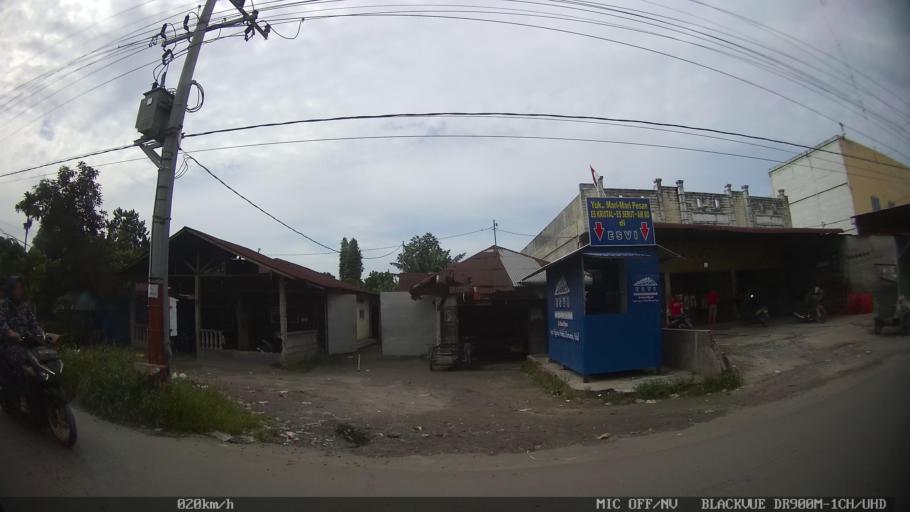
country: ID
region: North Sumatra
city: Medan
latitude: 3.6197
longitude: 98.7430
